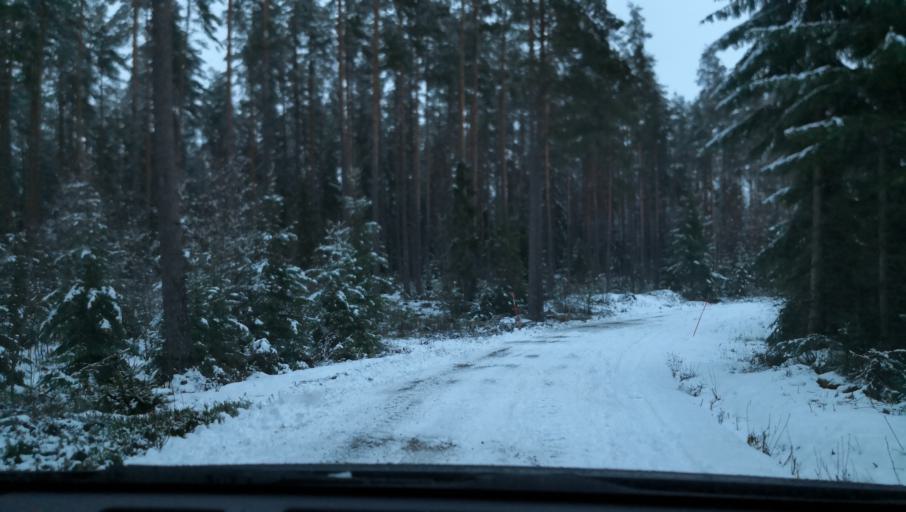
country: SE
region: Vaestmanland
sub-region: Kopings Kommun
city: Kolsva
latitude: 59.5657
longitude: 15.8244
